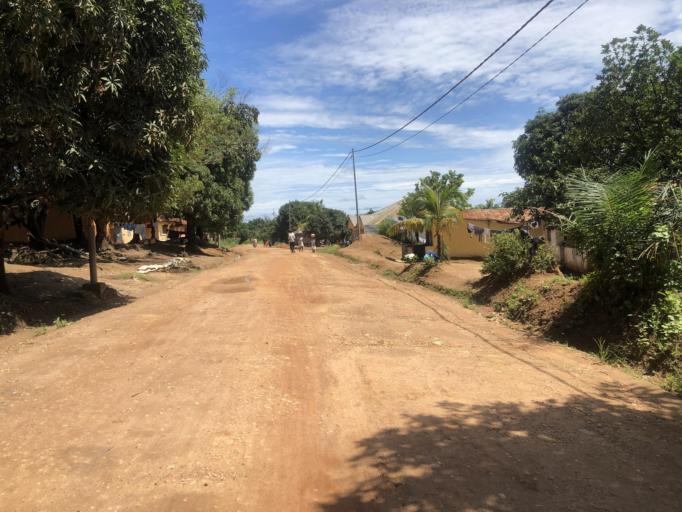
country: SL
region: Eastern Province
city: Koidu
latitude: 8.6410
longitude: -10.9547
